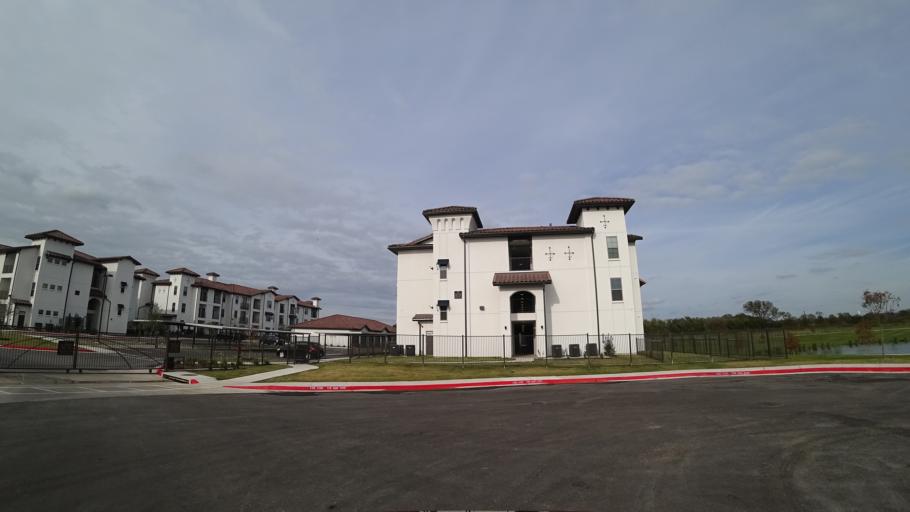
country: US
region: Texas
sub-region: Travis County
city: Wells Branch
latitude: 30.4333
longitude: -97.6657
